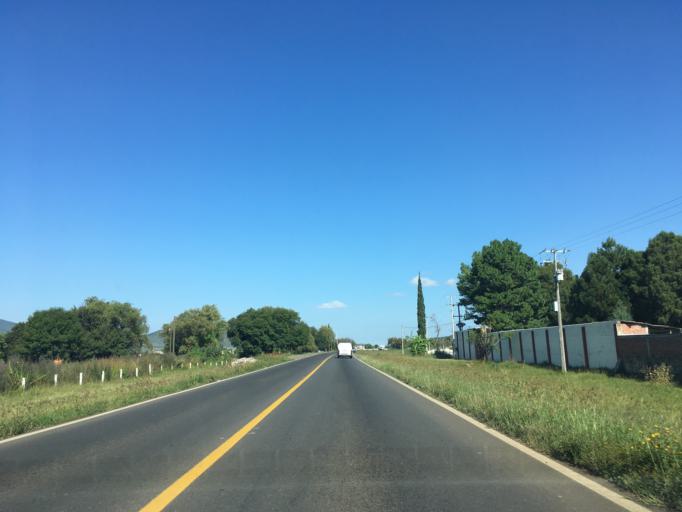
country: MX
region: Mexico
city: Tangancicuaro de Arista
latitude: 19.8719
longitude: -102.1961
